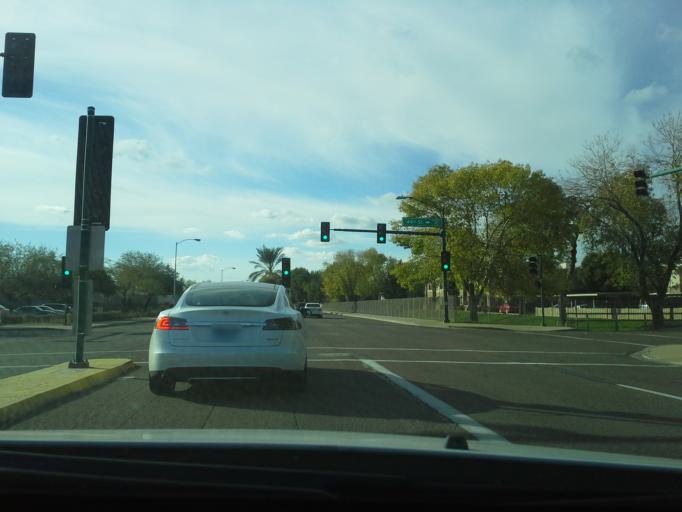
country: US
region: Arizona
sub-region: Maricopa County
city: Paradise Valley
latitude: 33.6050
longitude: -111.9819
